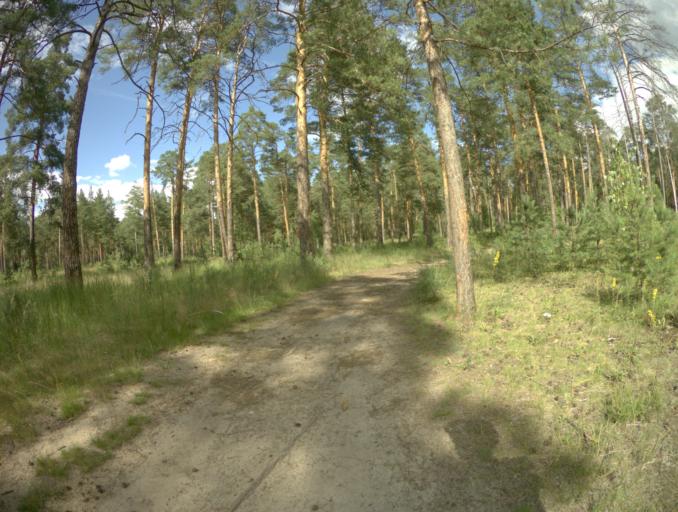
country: RU
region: Vladimir
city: Kommunar
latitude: 56.0958
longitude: 40.4399
